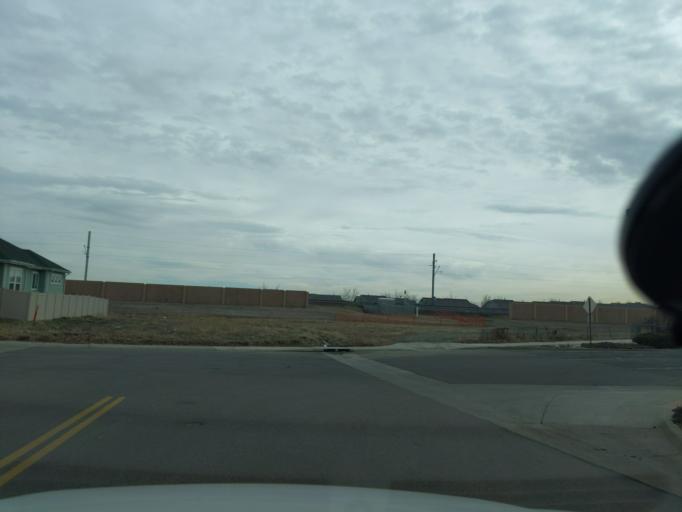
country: US
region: Colorado
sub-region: Adams County
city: Thornton
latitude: 39.8655
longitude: -104.9499
